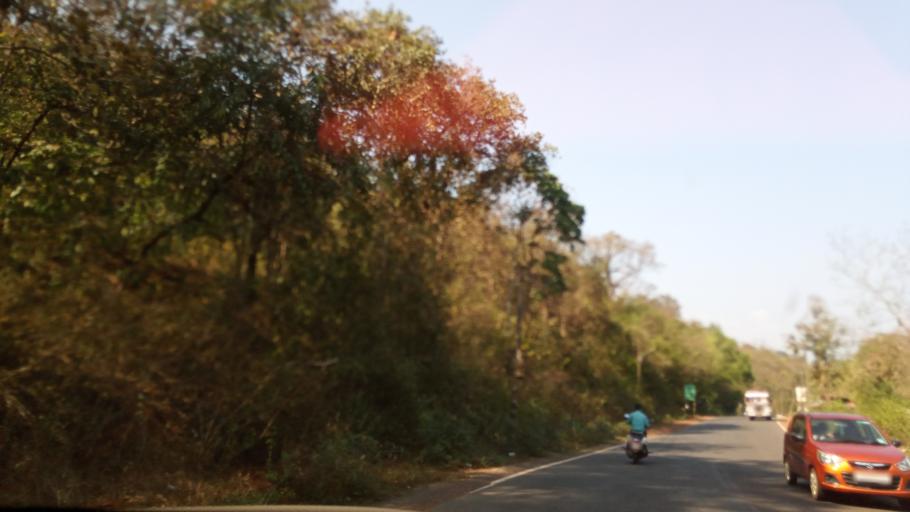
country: IN
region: Goa
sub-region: North Goa
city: Bandora
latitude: 15.4208
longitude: 73.9843
